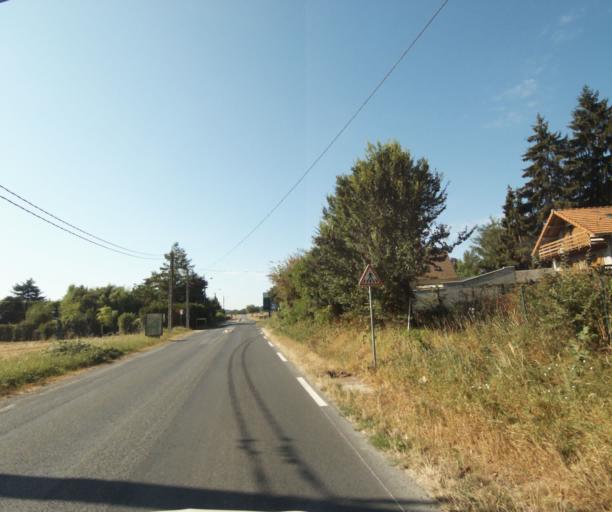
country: FR
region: Ile-de-France
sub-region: Departement de l'Essonne
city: Itteville
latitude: 48.5073
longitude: 2.3463
